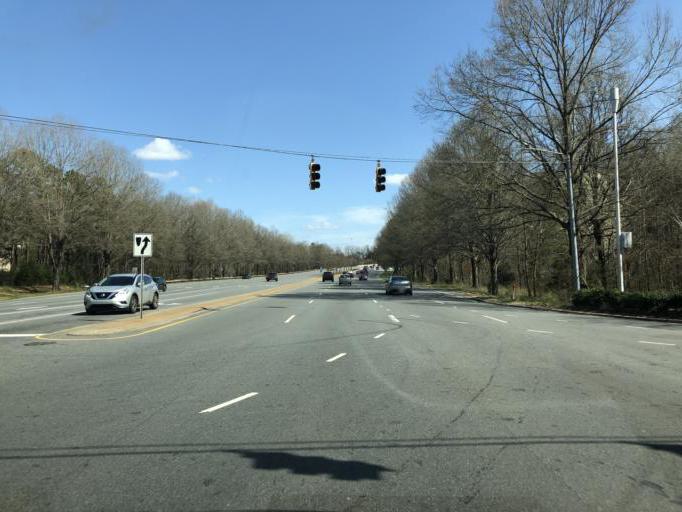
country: US
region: North Carolina
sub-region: Cabarrus County
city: Harrisburg
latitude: 35.3139
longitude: -80.7639
